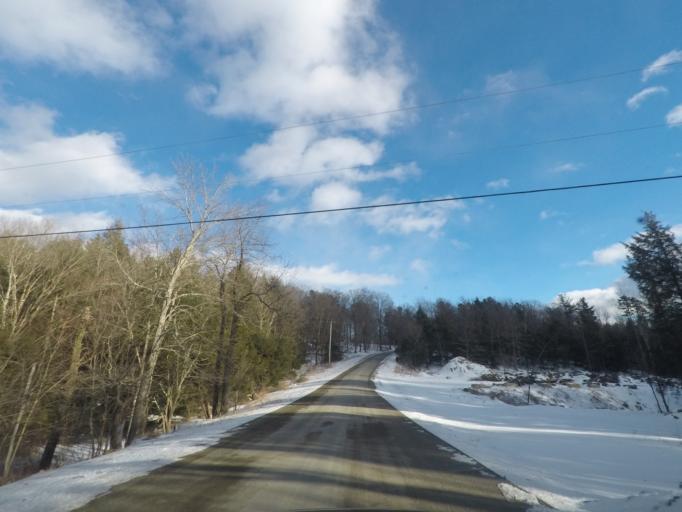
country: US
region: New York
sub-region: Rensselaer County
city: Poestenkill
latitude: 42.7434
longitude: -73.4770
